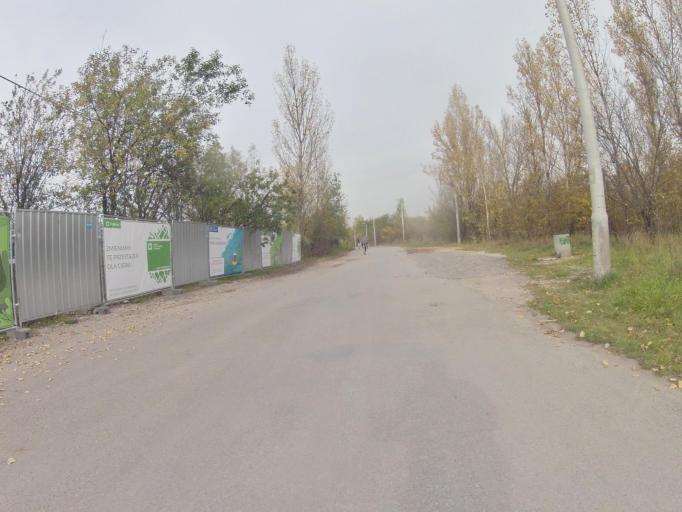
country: PL
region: Lesser Poland Voivodeship
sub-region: Krakow
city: Krakow
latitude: 50.0336
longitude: 19.9125
